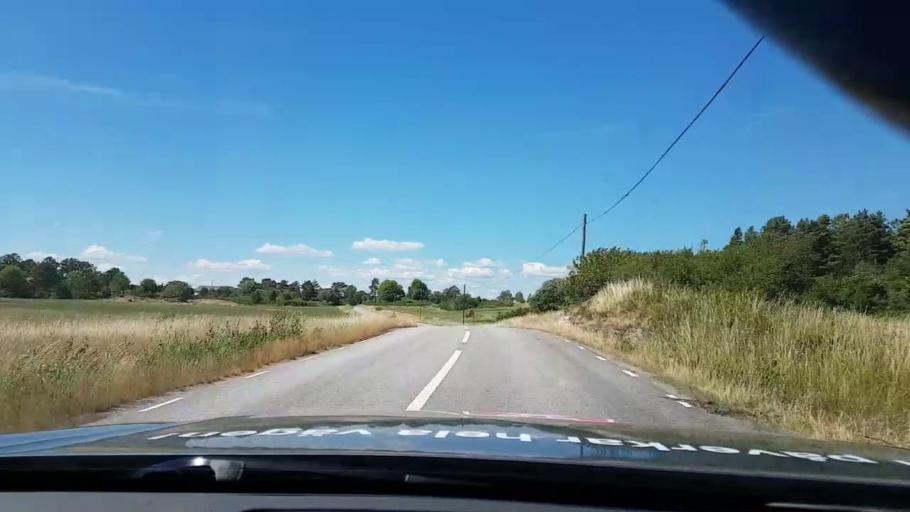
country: SE
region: Kalmar
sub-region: Vasterviks Kommun
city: Forserum
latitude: 57.9240
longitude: 16.5615
